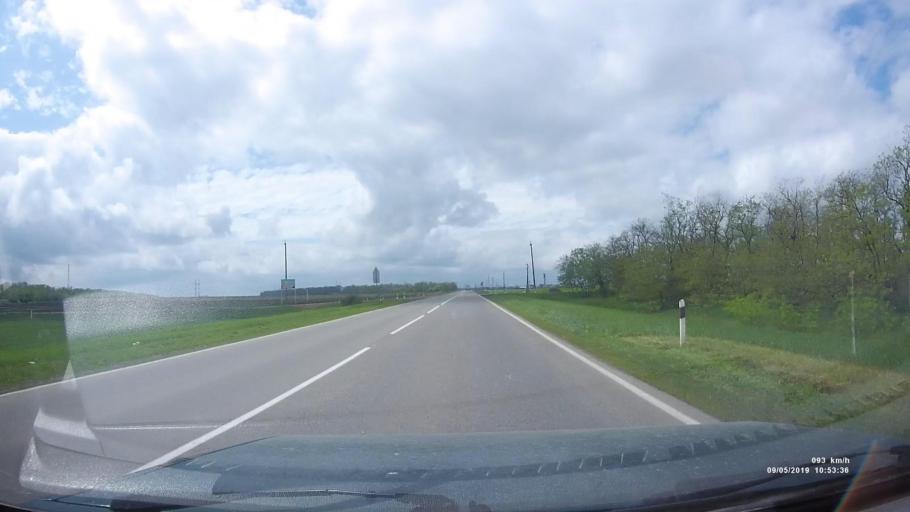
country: RU
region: Rostov
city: Peshkovo
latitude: 46.8872
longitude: 39.3399
